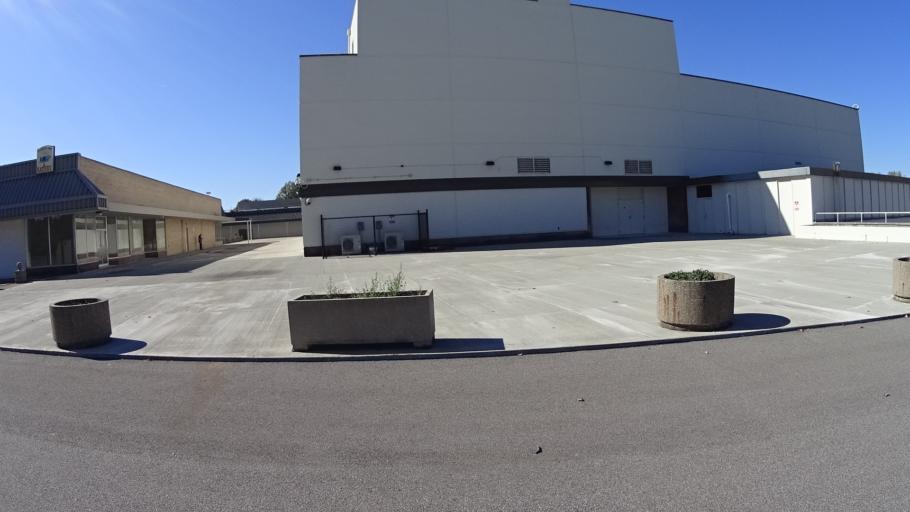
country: US
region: Ohio
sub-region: Lorain County
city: Lorain
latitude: 41.4208
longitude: -82.1501
